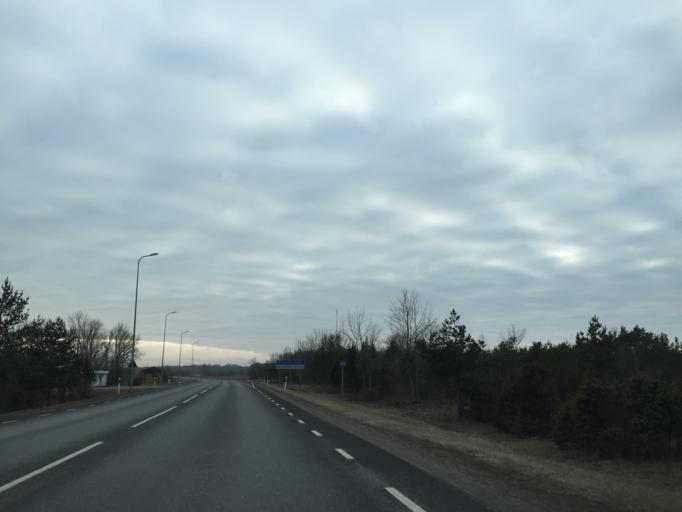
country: EE
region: Saare
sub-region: Orissaare vald
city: Orissaare
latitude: 58.5188
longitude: 22.8911
